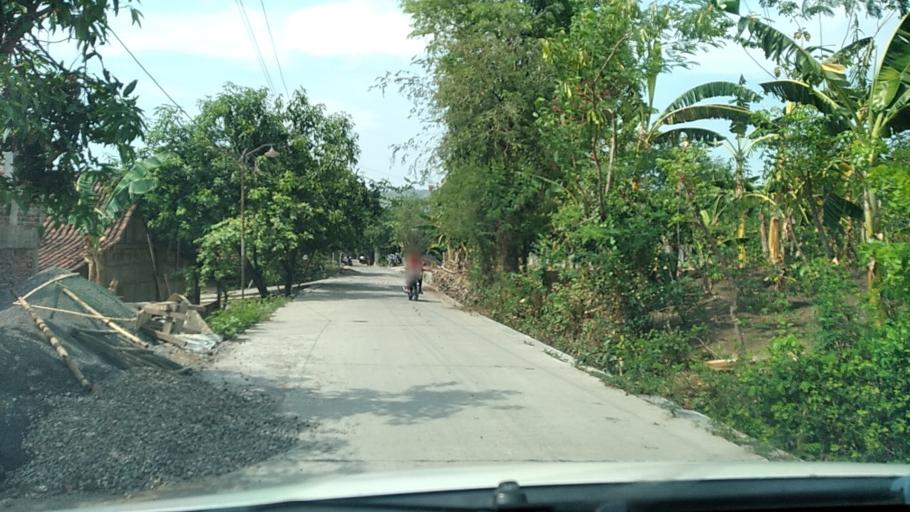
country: ID
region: Central Java
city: Mranggen
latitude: -7.0669
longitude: 110.4840
